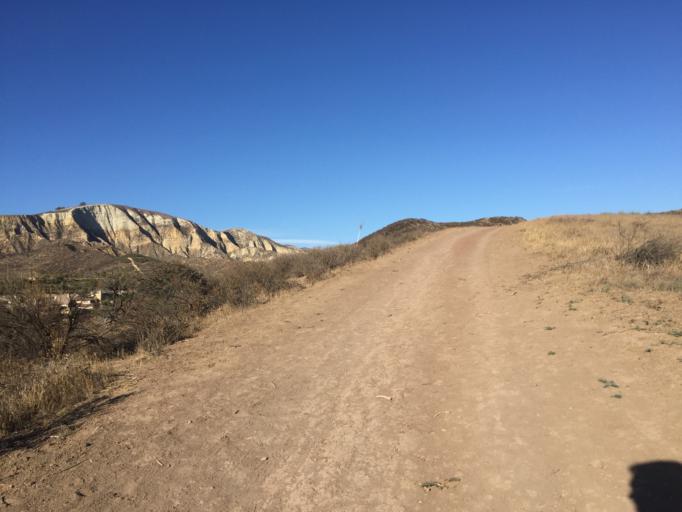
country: US
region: California
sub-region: Ventura County
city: Simi Valley
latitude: 34.3048
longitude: -118.7547
